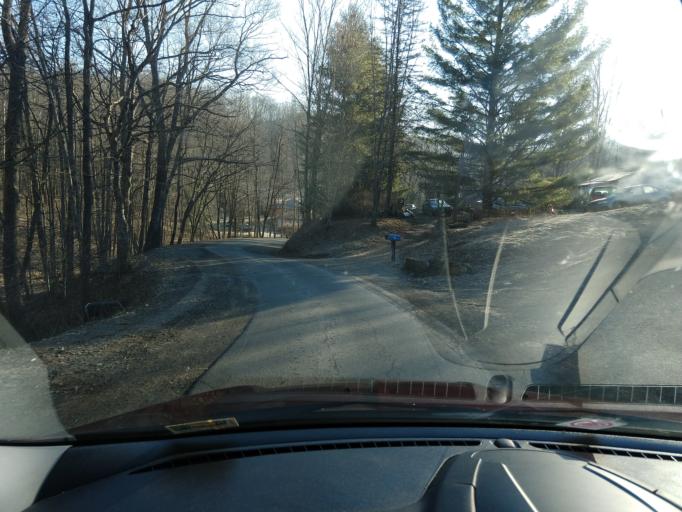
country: US
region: West Virginia
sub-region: Greenbrier County
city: Rainelle
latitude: 37.9263
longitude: -80.7334
